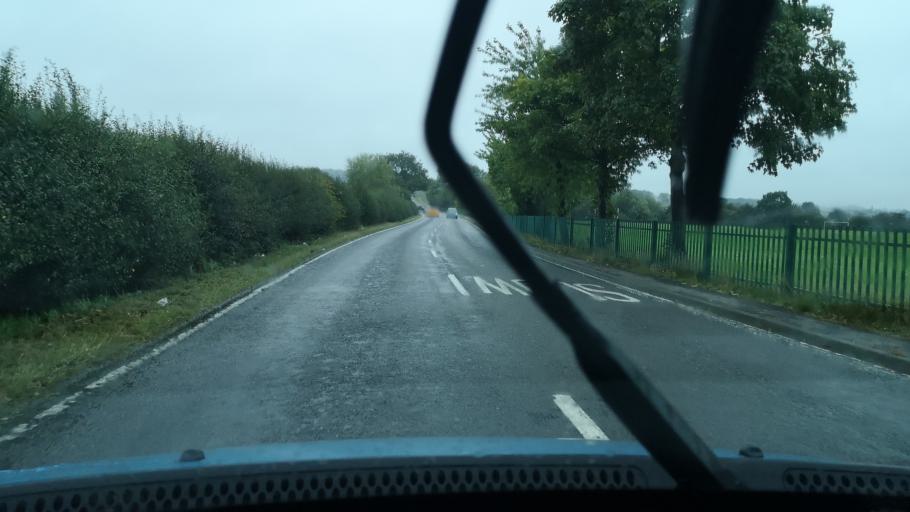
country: GB
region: England
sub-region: City and Borough of Wakefield
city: Low Ackworth
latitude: 53.6363
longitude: -1.3349
